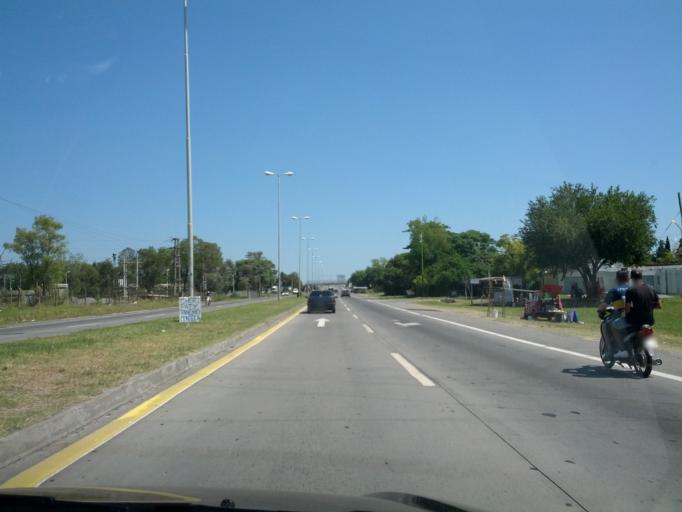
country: AR
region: Buenos Aires
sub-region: Partido de Campana
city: Campana
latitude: -34.1677
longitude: -58.9742
